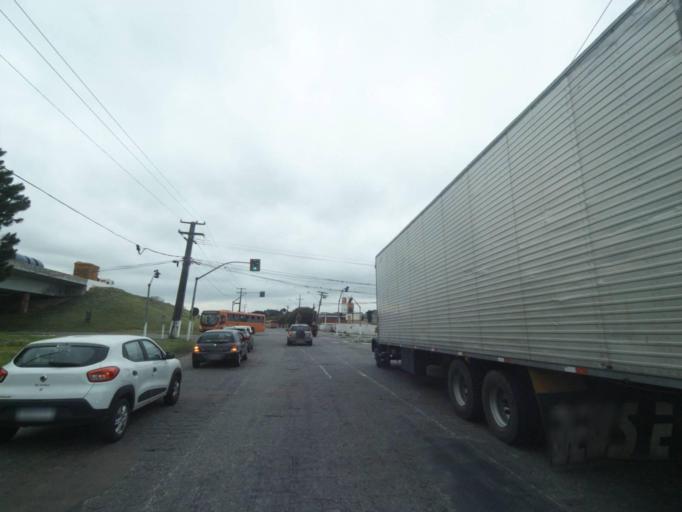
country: BR
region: Parana
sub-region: Sao Jose Dos Pinhais
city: Sao Jose dos Pinhais
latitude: -25.5345
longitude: -49.3164
